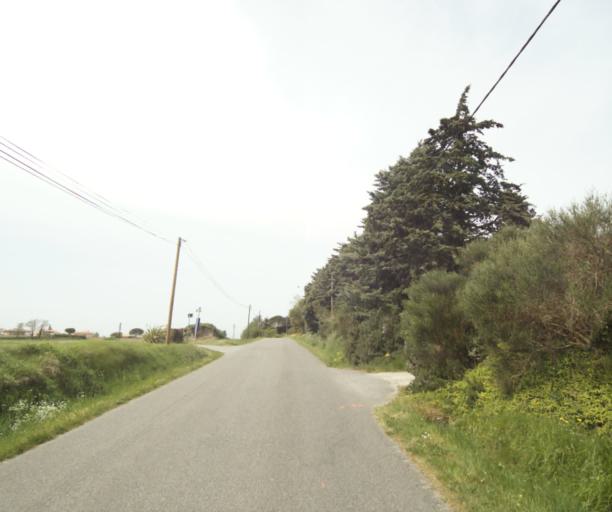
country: FR
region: Midi-Pyrenees
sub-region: Departement de la Haute-Garonne
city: Pompertuzat
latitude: 43.4843
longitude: 1.5088
